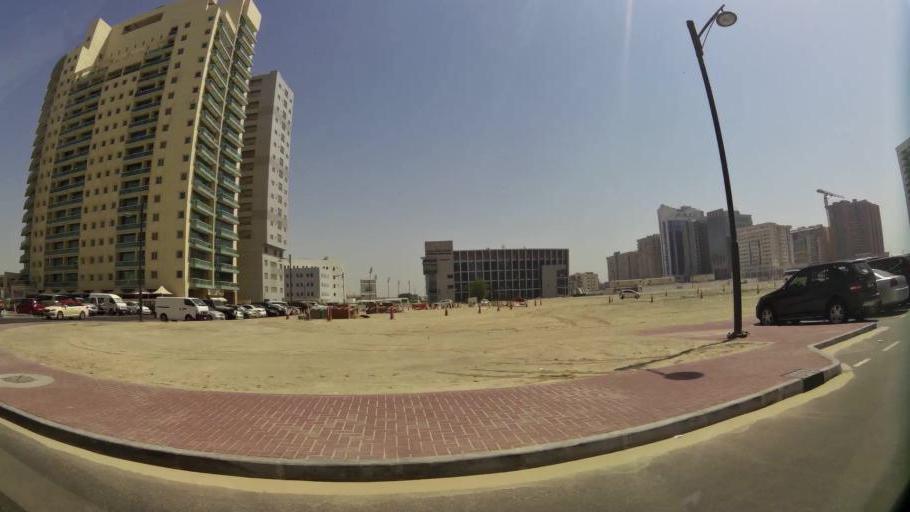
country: AE
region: Ash Shariqah
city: Sharjah
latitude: 25.2870
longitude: 55.3637
